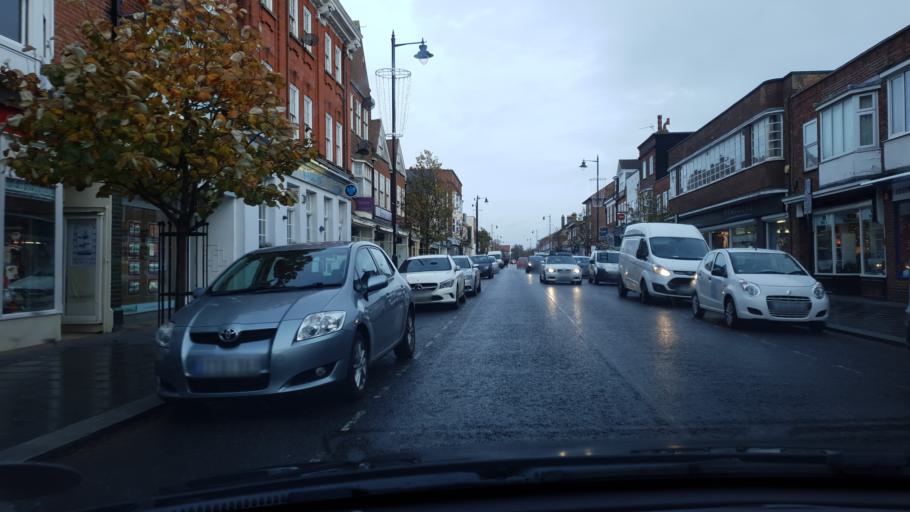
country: GB
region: England
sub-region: Essex
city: Frinton-on-Sea
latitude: 51.8317
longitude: 1.2454
